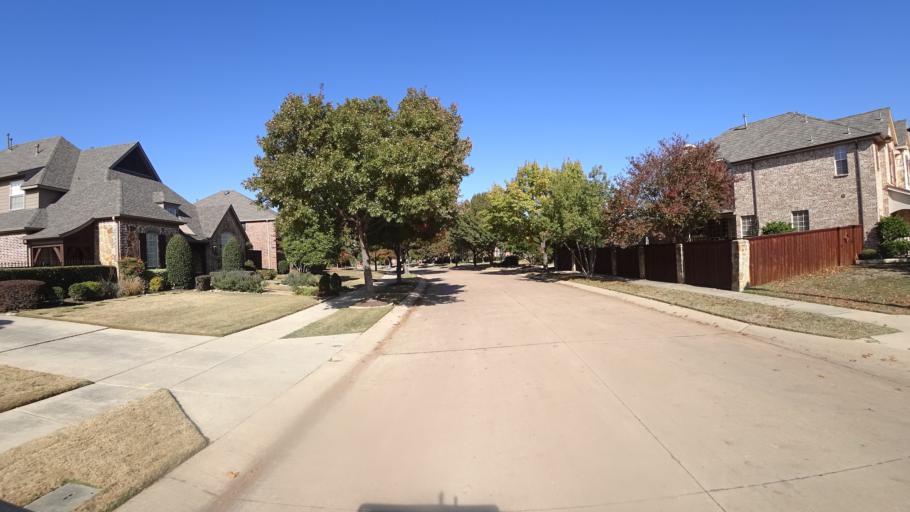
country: US
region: Texas
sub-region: Denton County
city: The Colony
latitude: 33.0324
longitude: -96.8891
